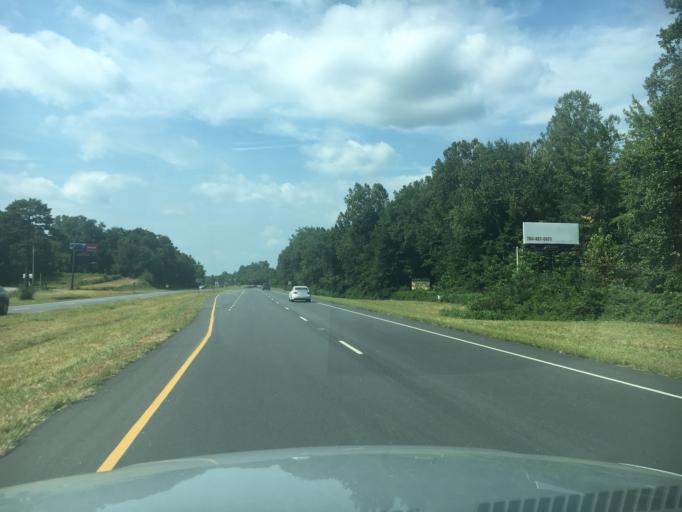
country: US
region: North Carolina
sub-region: Rutherford County
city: Forest City
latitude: 35.3242
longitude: -81.8849
